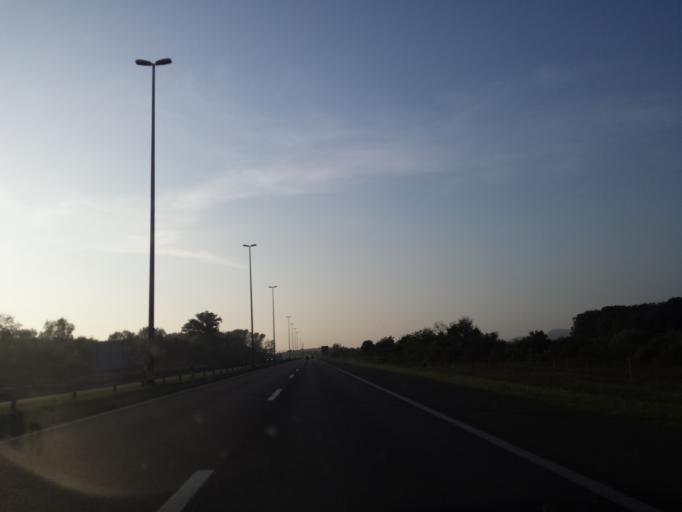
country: HR
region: Grad Zagreb
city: Lucko
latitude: 45.7802
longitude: 15.8691
